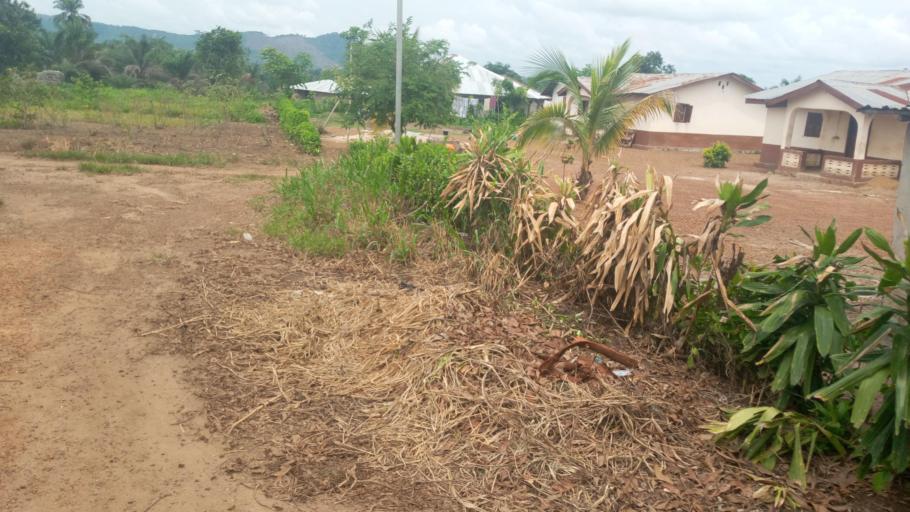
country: SL
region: Southern Province
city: Mogbwemo
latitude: 7.7744
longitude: -12.3013
